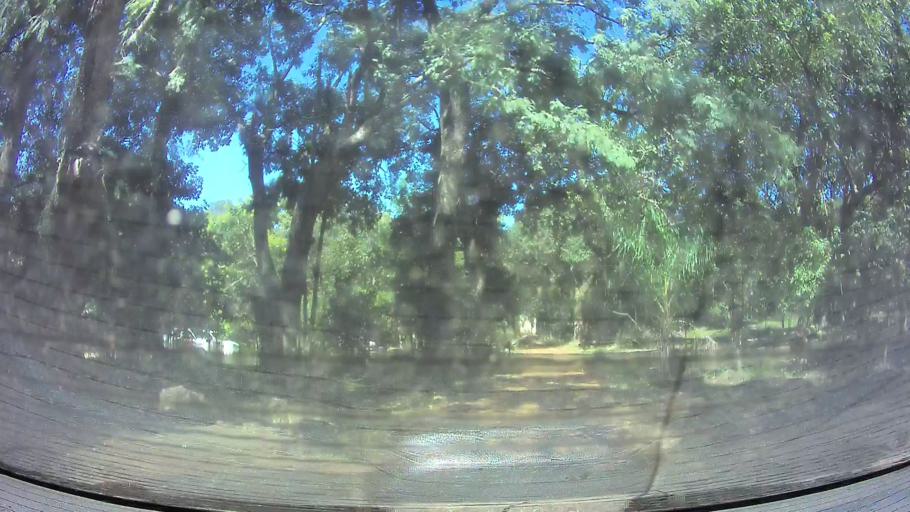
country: PY
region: Cordillera
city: Arroyos y Esteros
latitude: -24.9759
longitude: -57.2141
